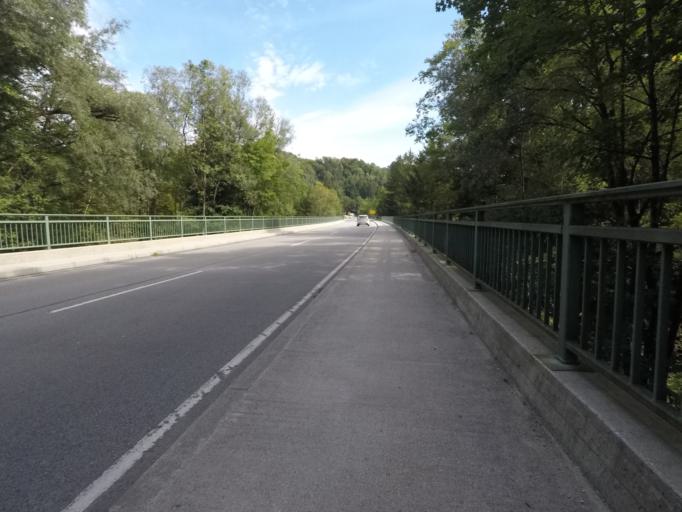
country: DE
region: Bavaria
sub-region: Upper Bavaria
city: Geretsried
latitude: 47.8567
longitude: 11.5116
